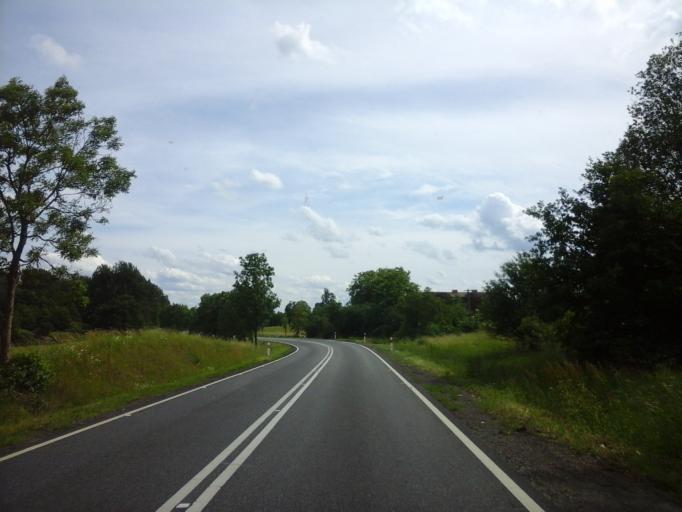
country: PL
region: West Pomeranian Voivodeship
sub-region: Powiat stargardzki
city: Insko
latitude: 53.4722
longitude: 15.5779
